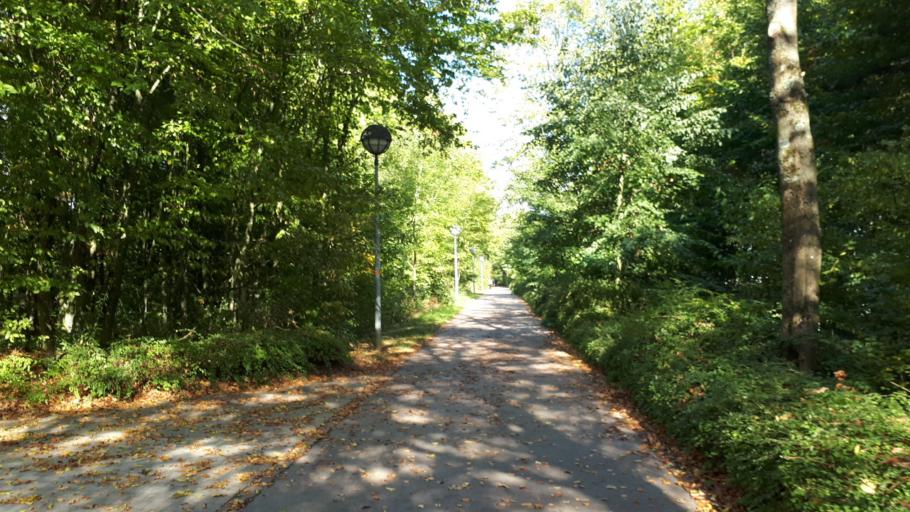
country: LU
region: Luxembourg
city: Kirchberg
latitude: 49.6288
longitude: 6.1604
